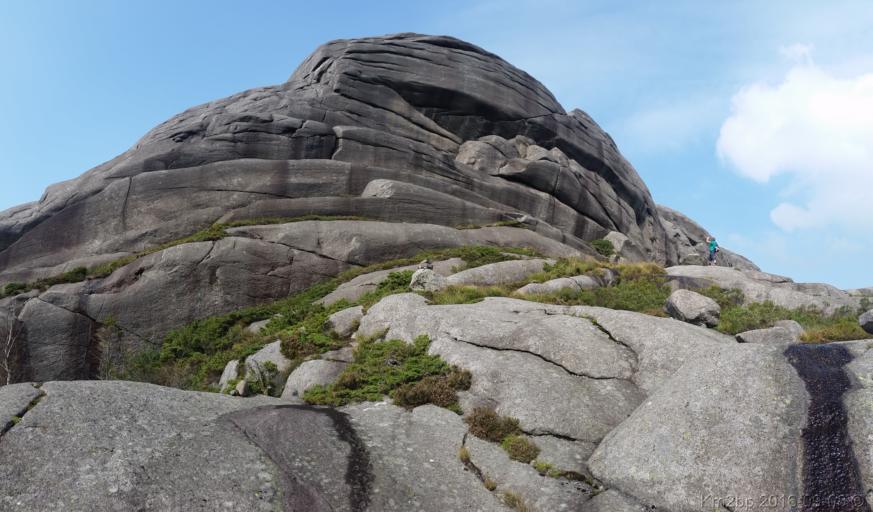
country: NO
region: Rogaland
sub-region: Sokndal
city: Hauge i Dalane
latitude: 58.3286
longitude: 6.3447
